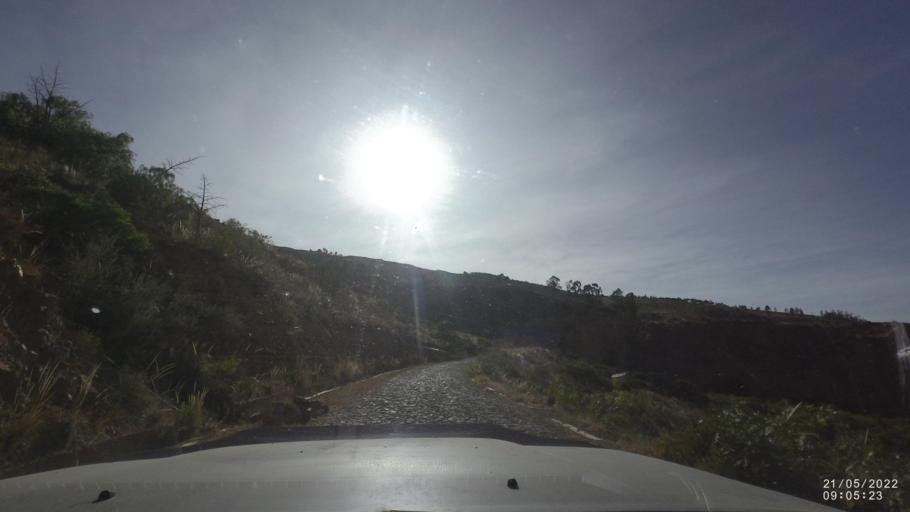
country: BO
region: Cochabamba
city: Cochabamba
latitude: -17.3795
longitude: -66.0224
